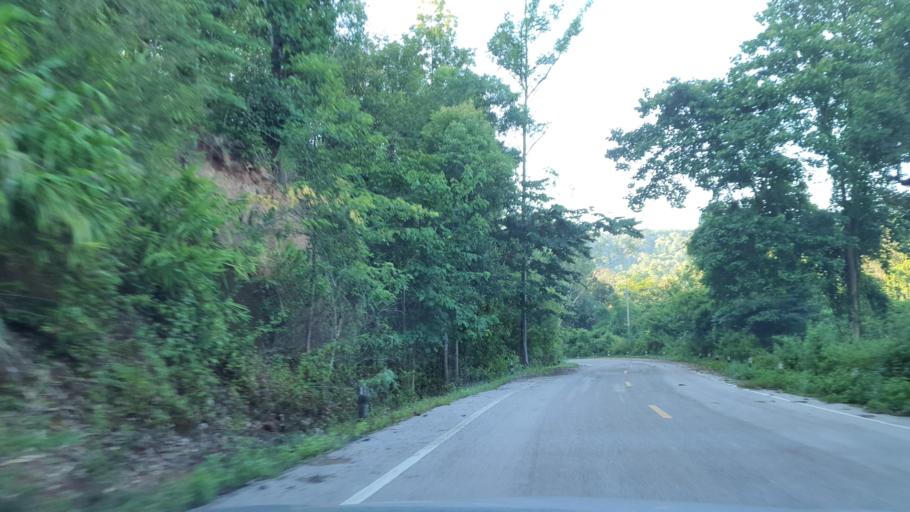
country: TH
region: Chiang Mai
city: Mae On
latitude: 18.8160
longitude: 99.3047
